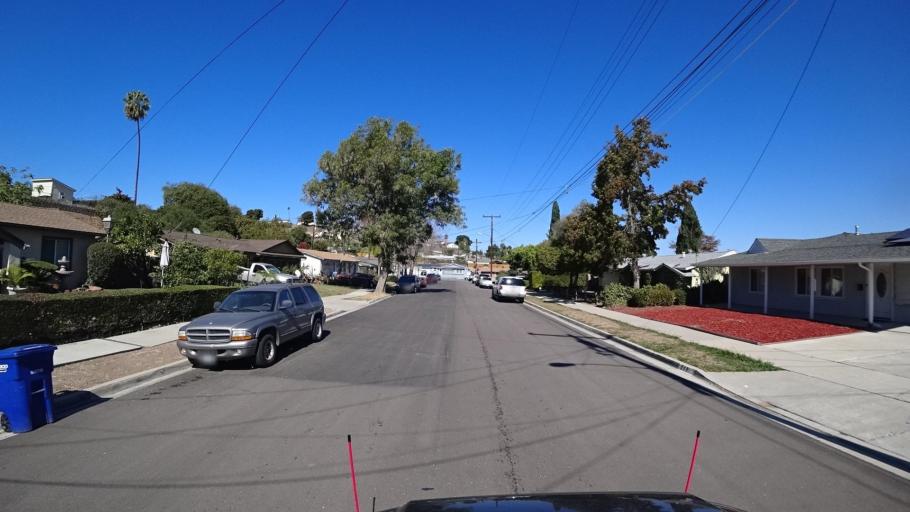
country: US
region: California
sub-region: San Diego County
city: La Presa
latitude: 32.7030
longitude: -117.0193
